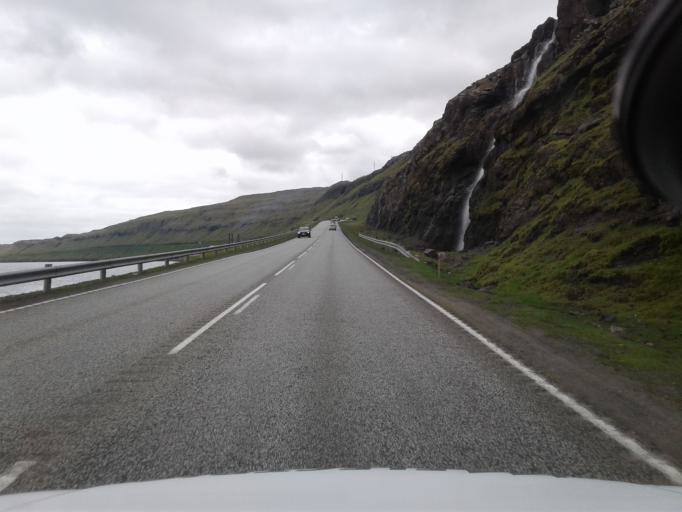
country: FO
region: Streymoy
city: Kollafjordhur
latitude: 62.0546
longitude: -6.8710
